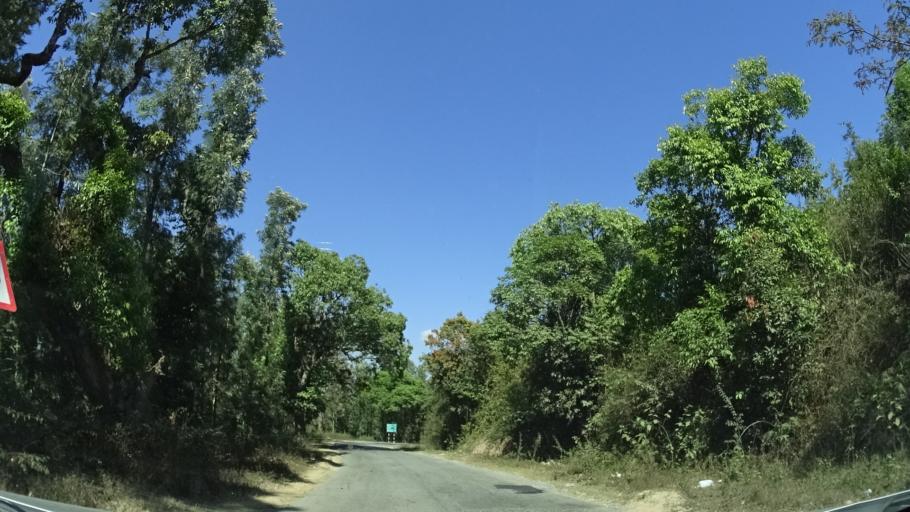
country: IN
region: Karnataka
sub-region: Chikmagalur
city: Mudigere
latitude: 13.1972
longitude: 75.6695
